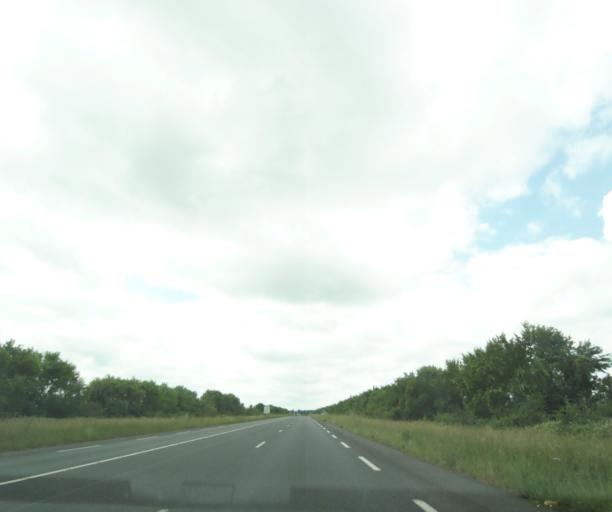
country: FR
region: Poitou-Charentes
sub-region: Departement des Deux-Sevres
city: Saint-Varent
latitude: 46.8818
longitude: -0.1953
